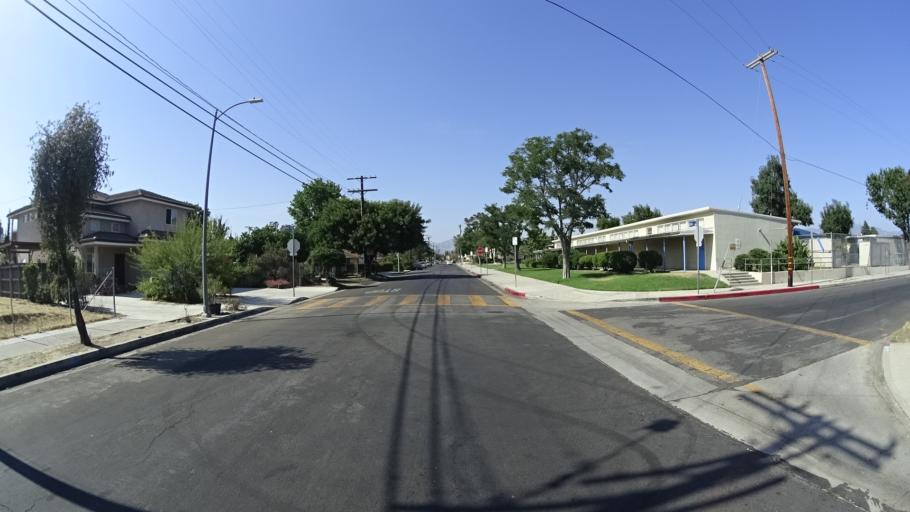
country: US
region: California
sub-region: Los Angeles County
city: Van Nuys
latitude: 34.2121
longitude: -118.4170
